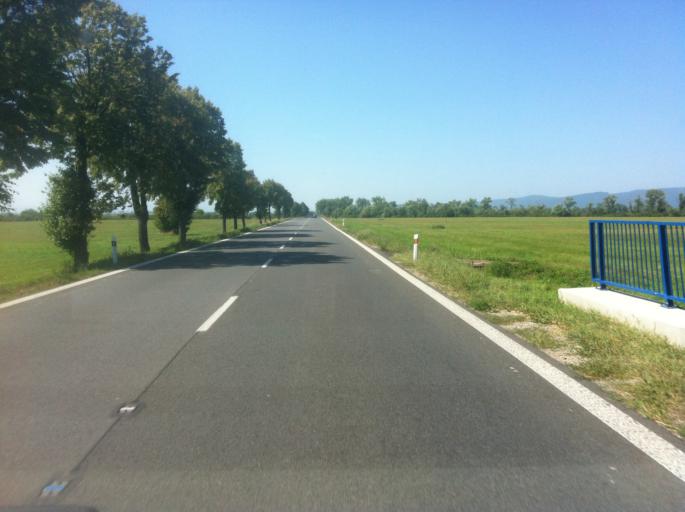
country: SK
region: Kosicky
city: Sobrance
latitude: 48.7583
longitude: 22.1343
